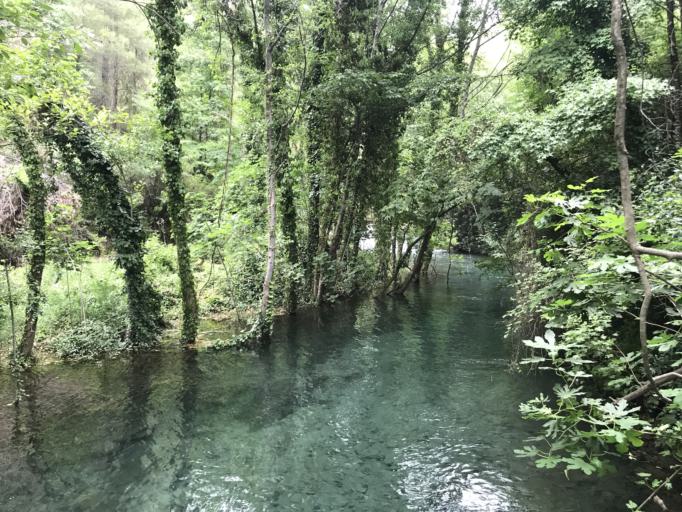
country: TR
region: Mugla
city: Ortaca
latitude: 36.9229
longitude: 28.8012
